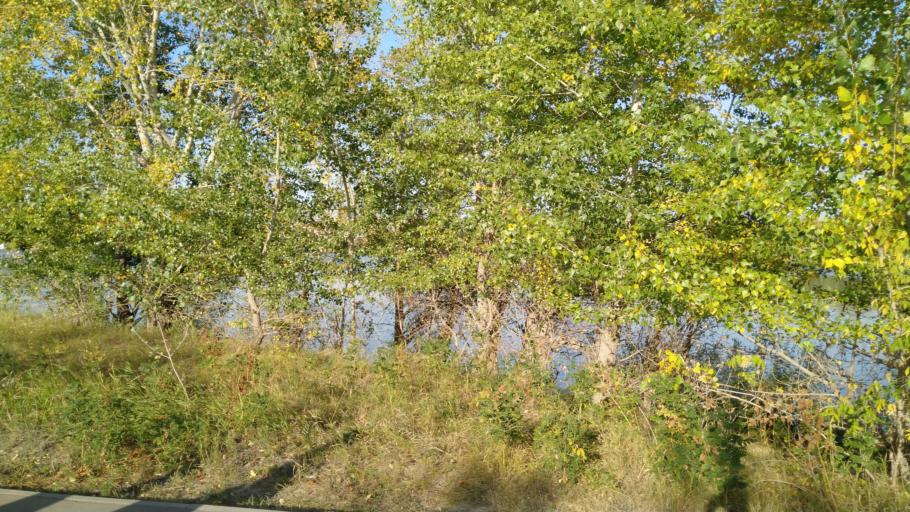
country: KZ
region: Pavlodar
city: Pavlodar
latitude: 52.2613
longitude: 76.9332
